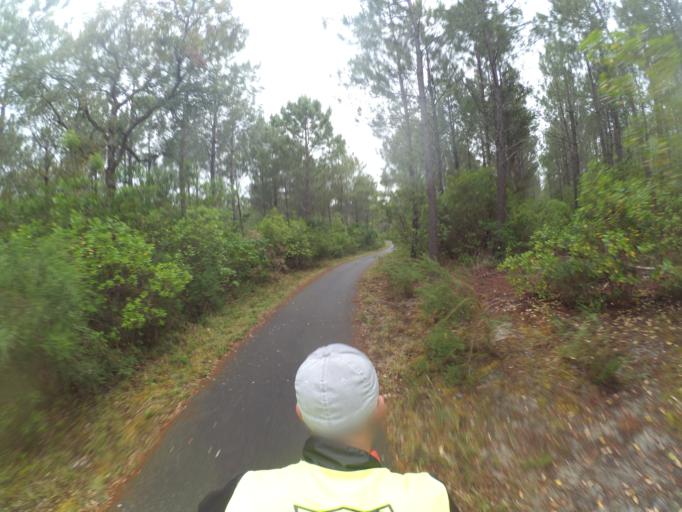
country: FR
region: Aquitaine
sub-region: Departement des Landes
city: Mimizan
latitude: 44.2214
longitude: -1.2554
